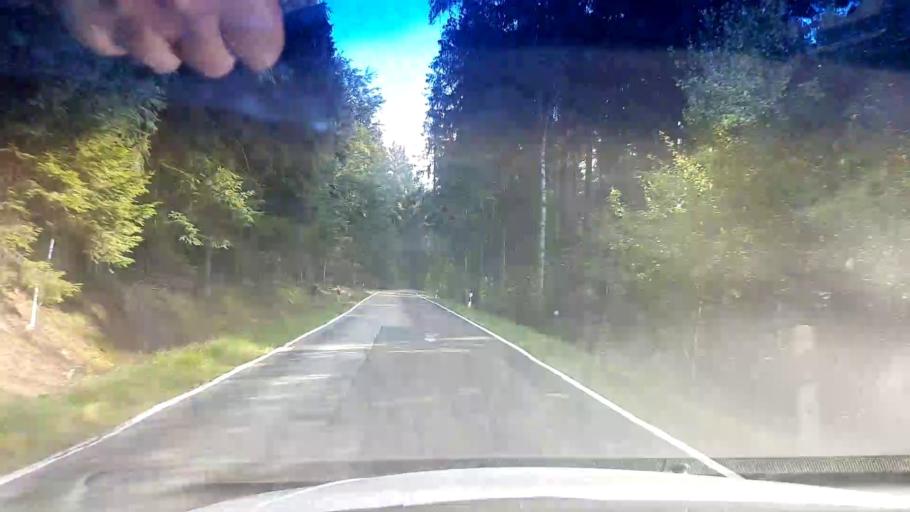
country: DE
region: Bavaria
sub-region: Upper Palatinate
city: Neualbenreuth
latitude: 49.9230
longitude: 12.4056
